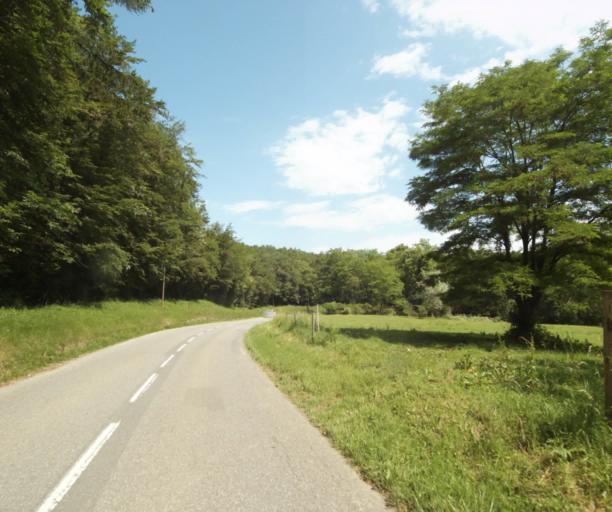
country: FR
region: Rhone-Alpes
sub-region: Departement de la Haute-Savoie
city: Armoy
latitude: 46.3575
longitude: 6.5144
